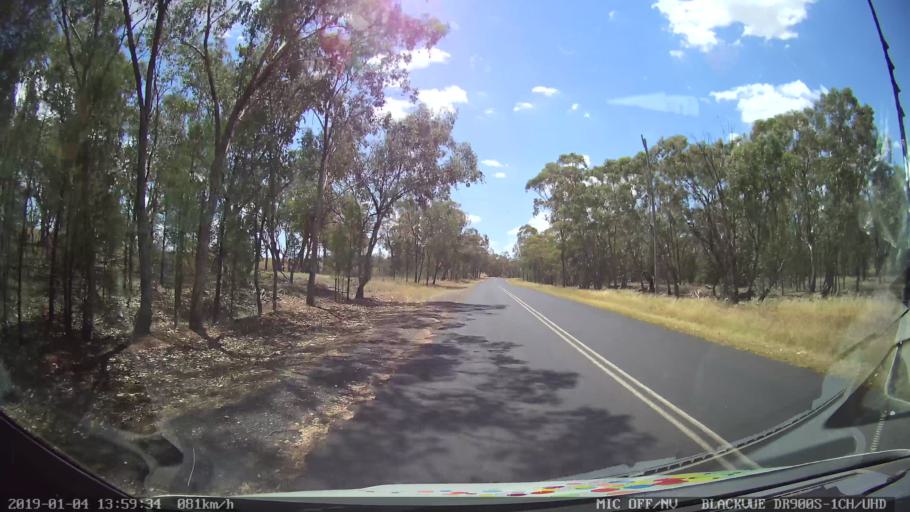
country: AU
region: New South Wales
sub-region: Dubbo Municipality
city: Dubbo
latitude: -32.3155
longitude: 148.5888
